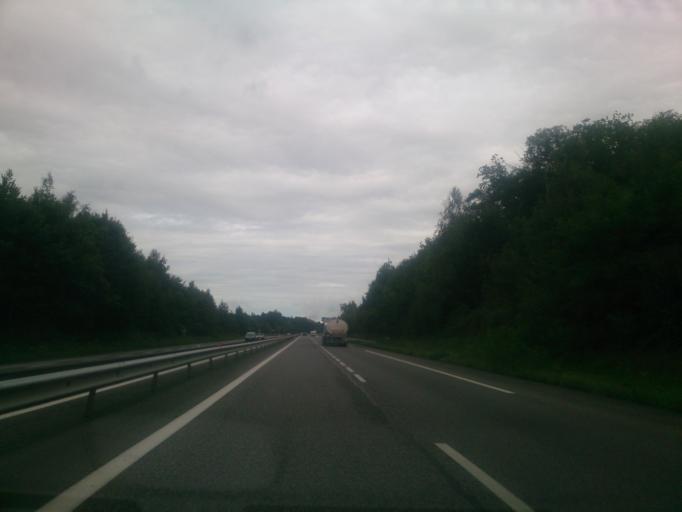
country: FR
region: Midi-Pyrenees
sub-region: Departement de la Haute-Garonne
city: Montrejeau
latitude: 43.1023
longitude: 0.4802
